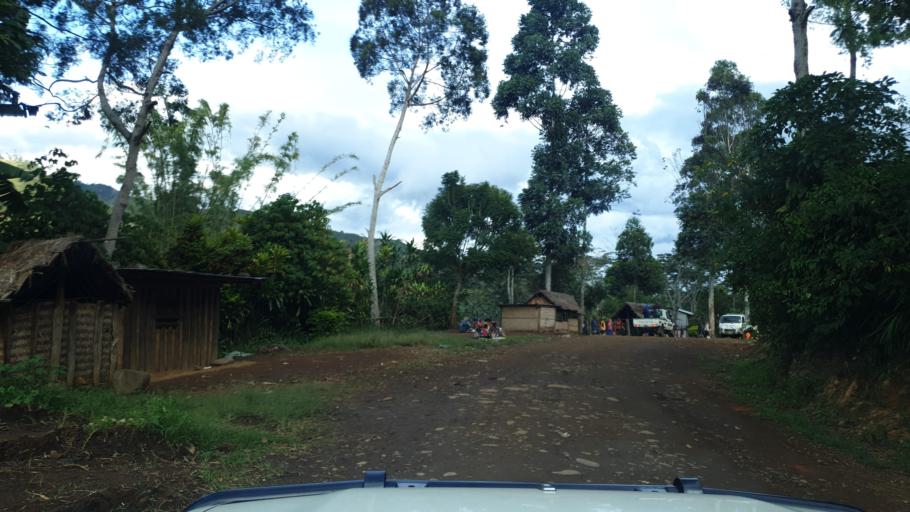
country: PG
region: Eastern Highlands
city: Goroka
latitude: -5.9373
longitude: 145.2673
